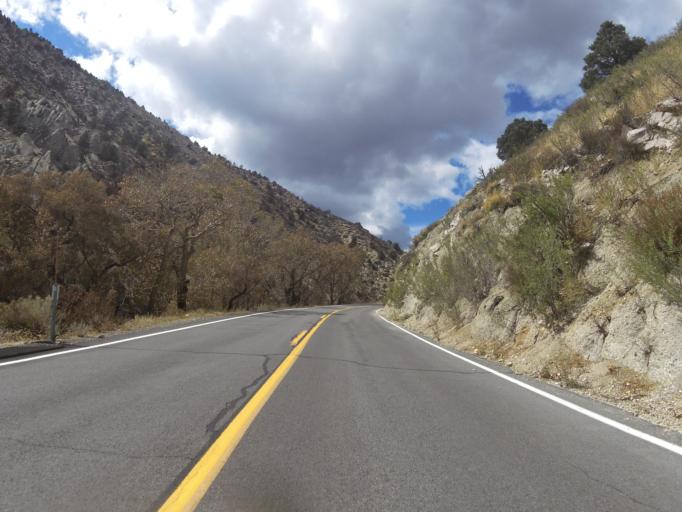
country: US
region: Nevada
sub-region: Lyon County
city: Smith Valley
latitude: 38.6420
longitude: -119.5319
